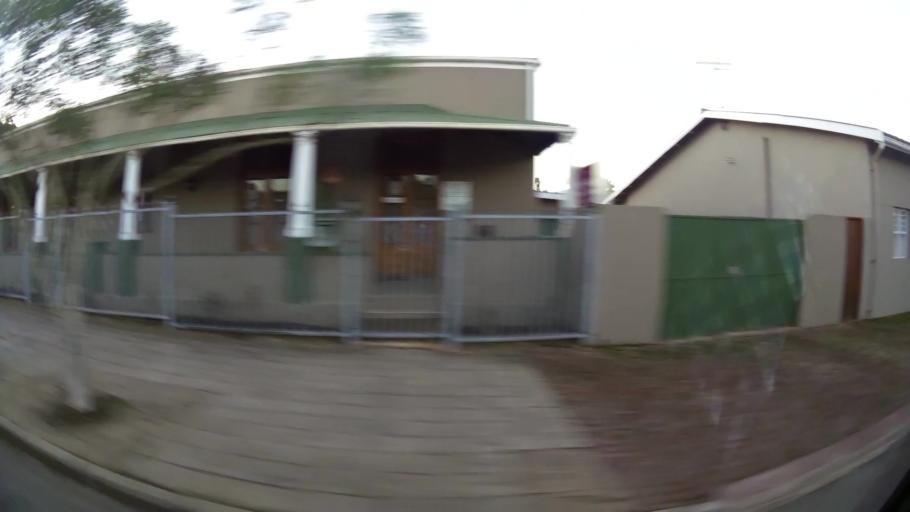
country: ZA
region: Western Cape
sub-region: Eden District Municipality
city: Riversdale
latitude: -34.0913
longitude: 21.2569
